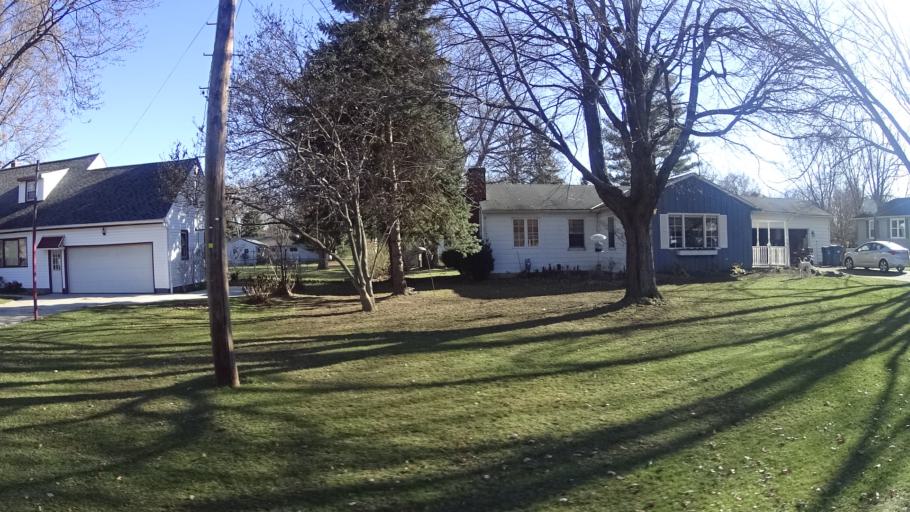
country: US
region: Ohio
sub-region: Lorain County
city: Elyria
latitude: 41.3984
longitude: -82.1483
